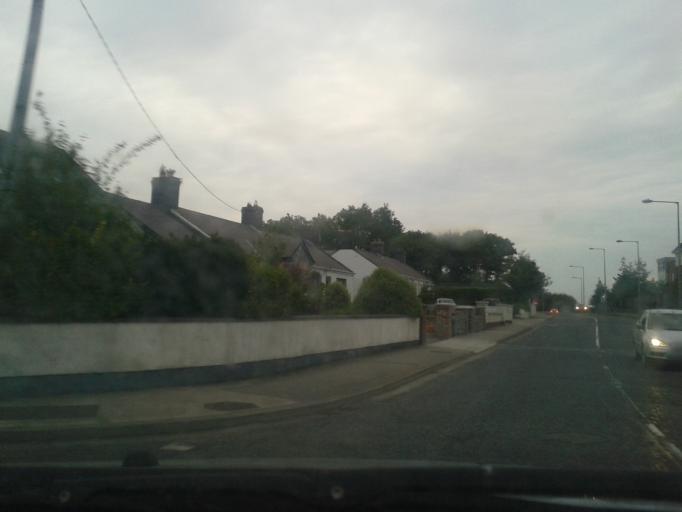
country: IE
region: Leinster
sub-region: Fingal County
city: Swords
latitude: 53.4462
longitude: -6.2403
